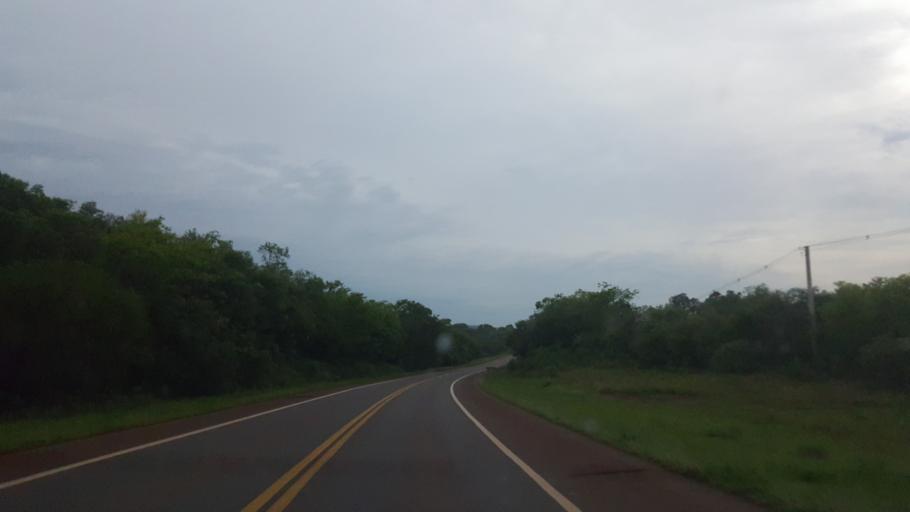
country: AR
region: Misiones
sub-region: Departamento de Apostoles
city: San Jose
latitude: -27.7658
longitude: -55.8008
